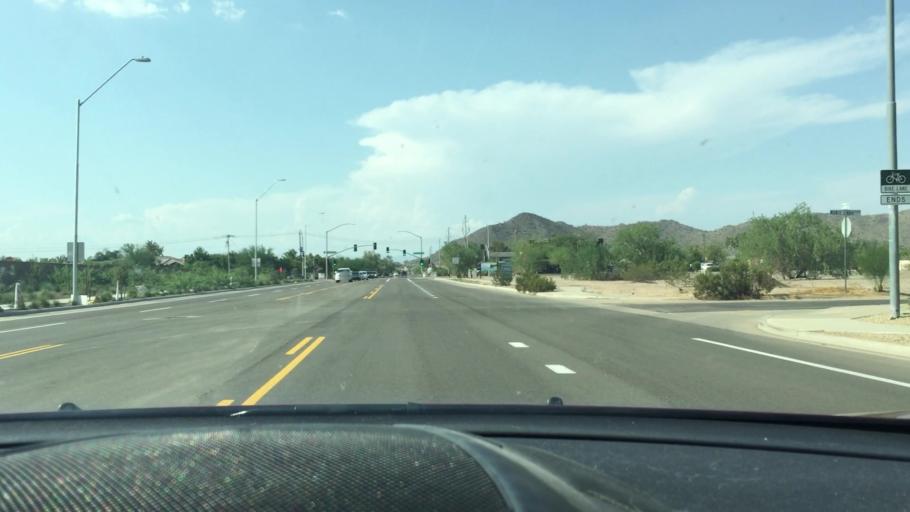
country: US
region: Arizona
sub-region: Maricopa County
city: Sun City West
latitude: 33.6947
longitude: -112.2551
